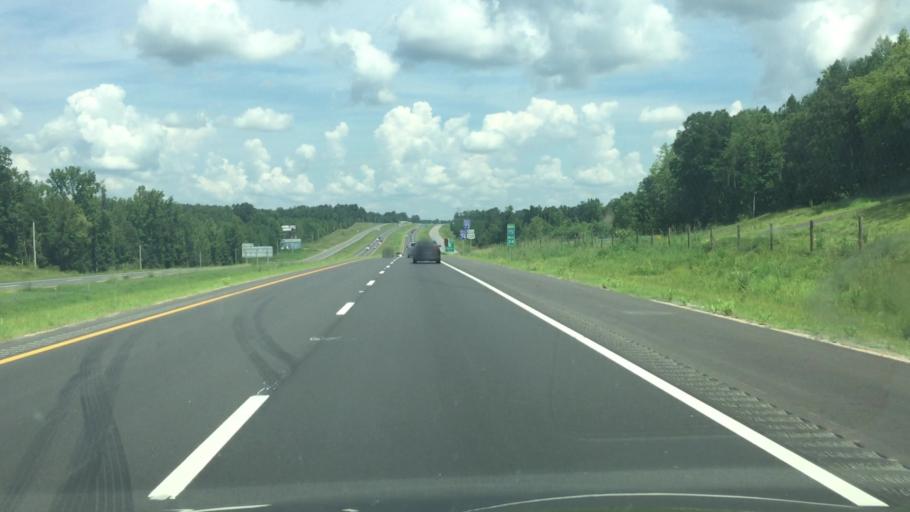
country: US
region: North Carolina
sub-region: Richmond County
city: Ellerbe
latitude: 35.0221
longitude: -79.7697
